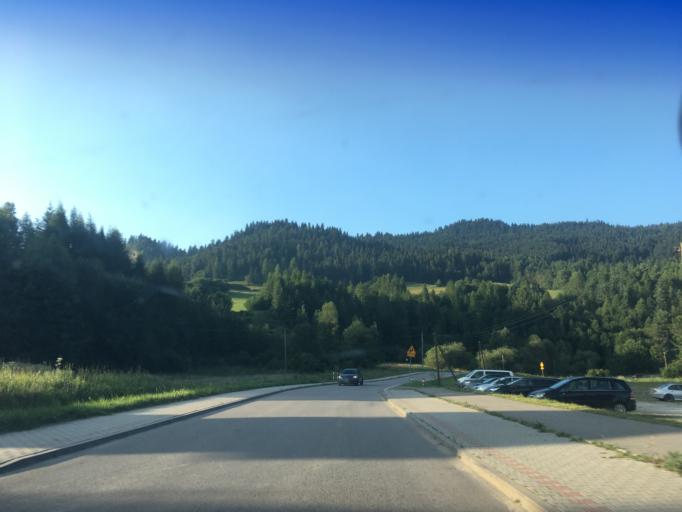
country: PL
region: Lesser Poland Voivodeship
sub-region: Powiat nowotarski
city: Krosnica
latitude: 49.4071
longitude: 20.3664
